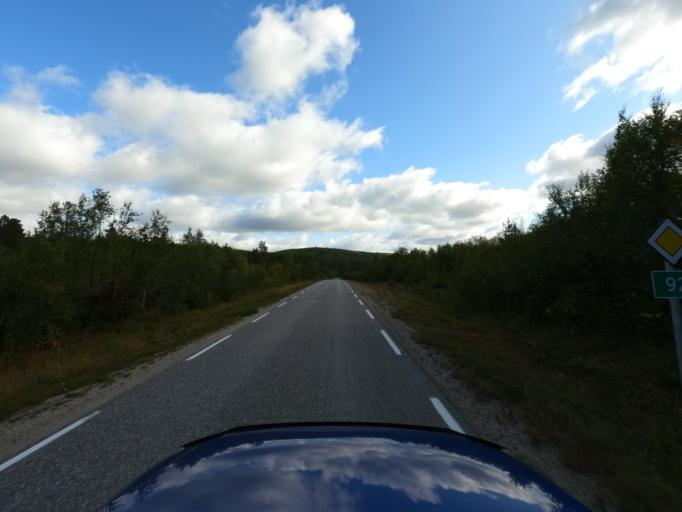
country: NO
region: Finnmark Fylke
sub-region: Karasjok
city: Karasjohka
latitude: 69.4299
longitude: 24.8872
